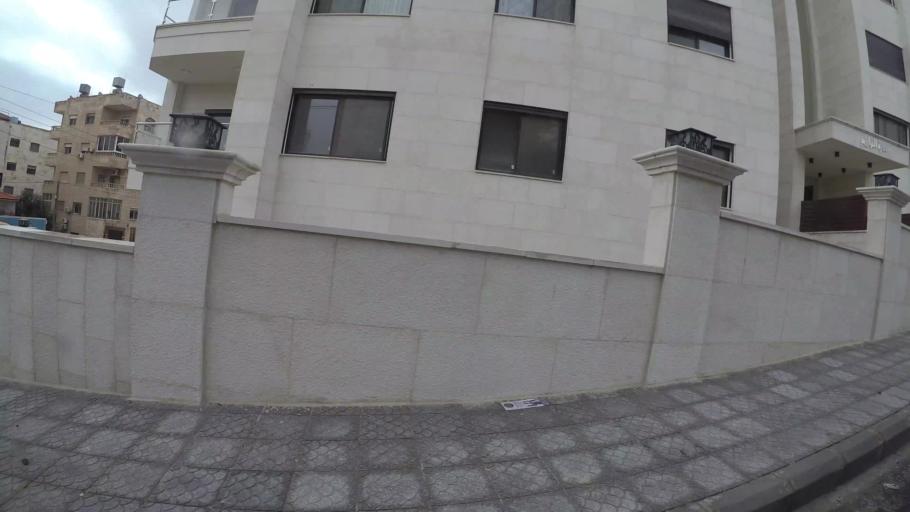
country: JO
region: Amman
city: Al Jubayhah
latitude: 31.9900
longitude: 35.8570
